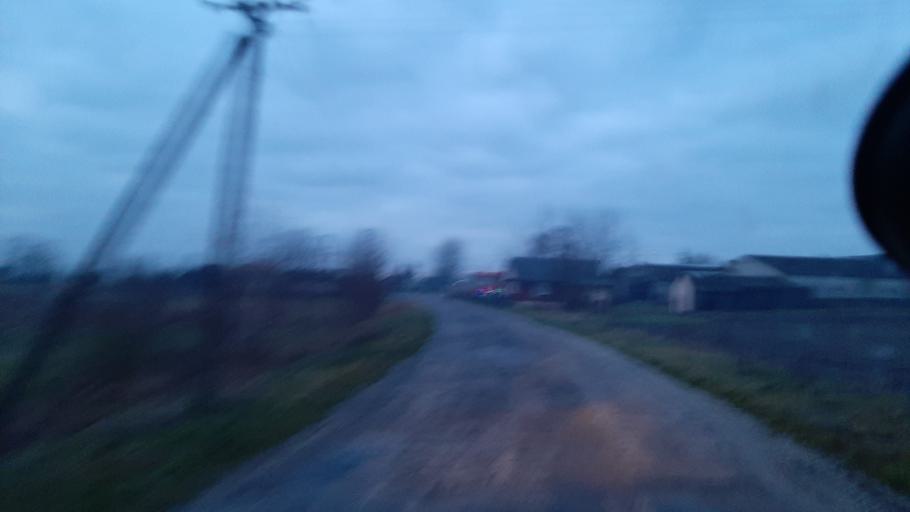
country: PL
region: Lublin Voivodeship
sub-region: Powiat lubartowski
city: Firlej
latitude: 51.6009
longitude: 22.5142
